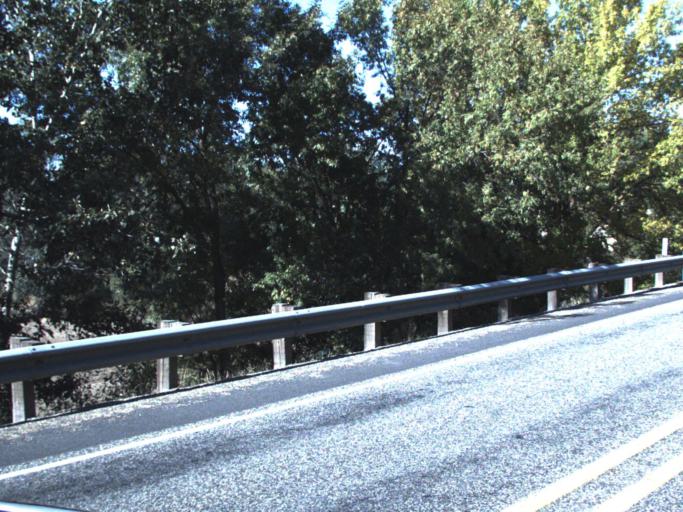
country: US
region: Washington
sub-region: Walla Walla County
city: Waitsburg
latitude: 46.2735
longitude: -118.2210
